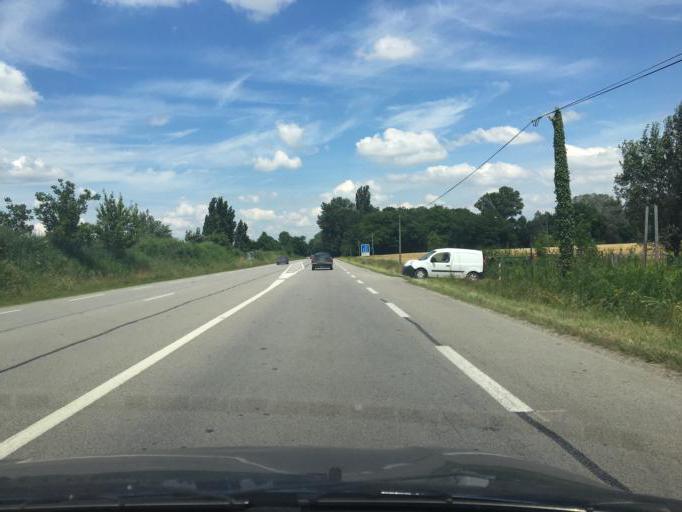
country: FR
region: Rhone-Alpes
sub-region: Departement de l'Ardeche
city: Charmes-sur-Rhone
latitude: 44.8638
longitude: 4.8580
